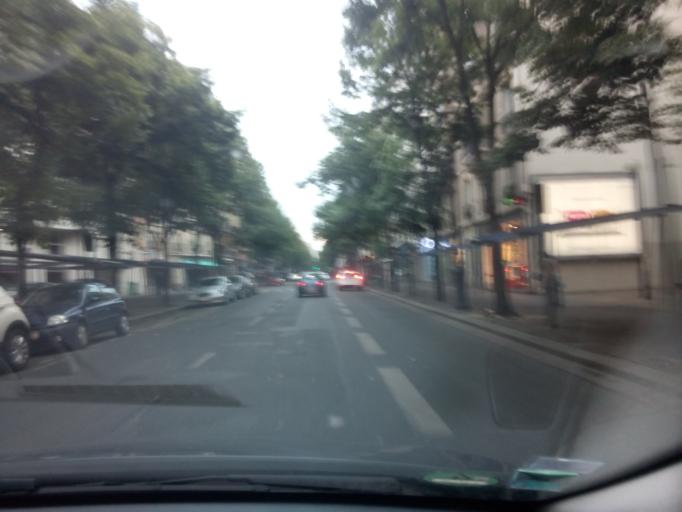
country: FR
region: Ile-de-France
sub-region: Departement des Hauts-de-Seine
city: Vanves
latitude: 48.8364
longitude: 2.2996
